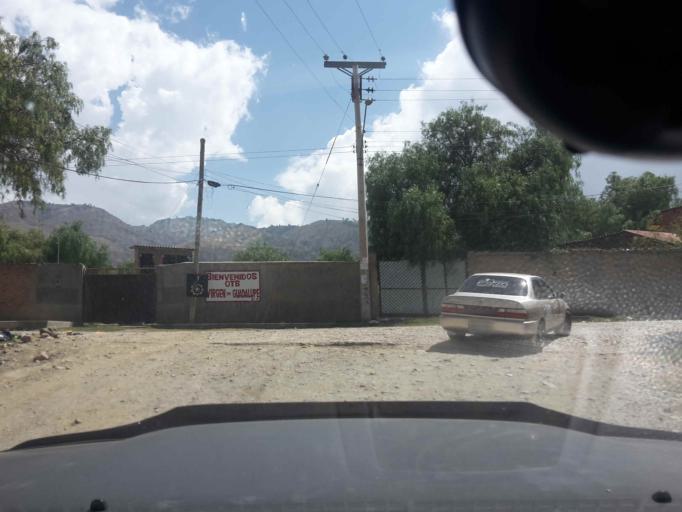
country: BO
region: Cochabamba
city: Cochabamba
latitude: -17.3870
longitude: -66.0683
